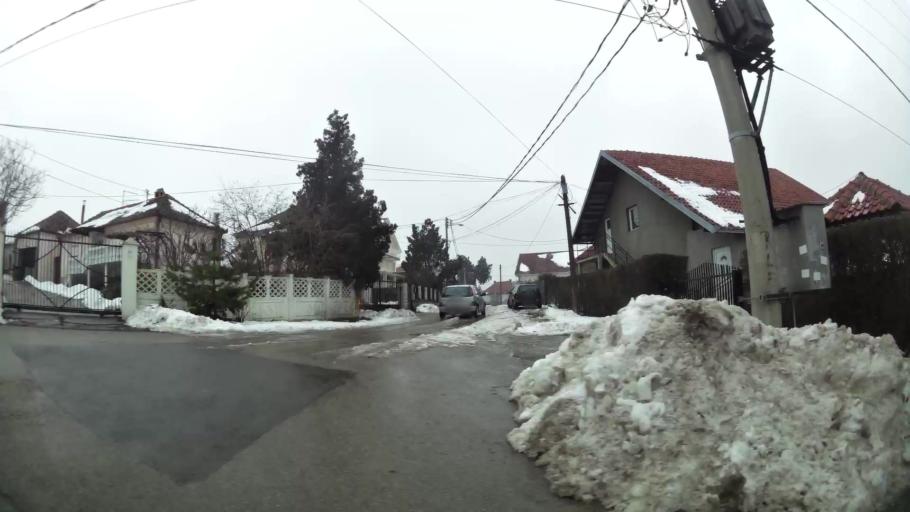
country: RS
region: Central Serbia
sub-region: Belgrade
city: Zvezdara
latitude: 44.7607
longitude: 20.5199
